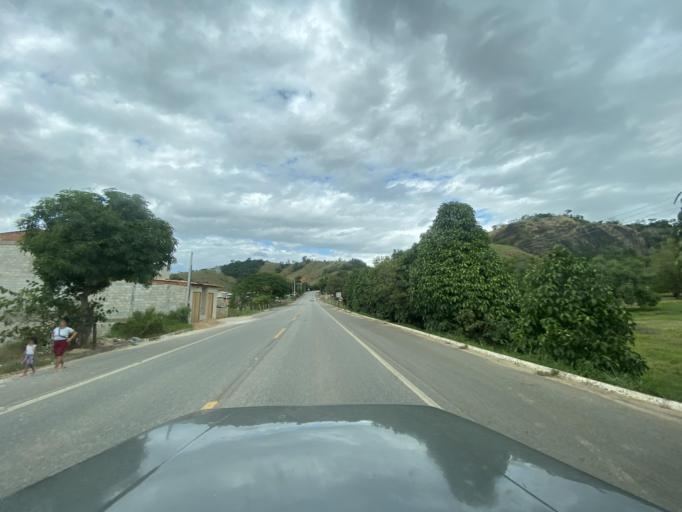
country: BR
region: Espirito Santo
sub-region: Jeronimo Monteiro
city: Jeronimo Monteiro
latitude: -20.7628
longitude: -41.4510
